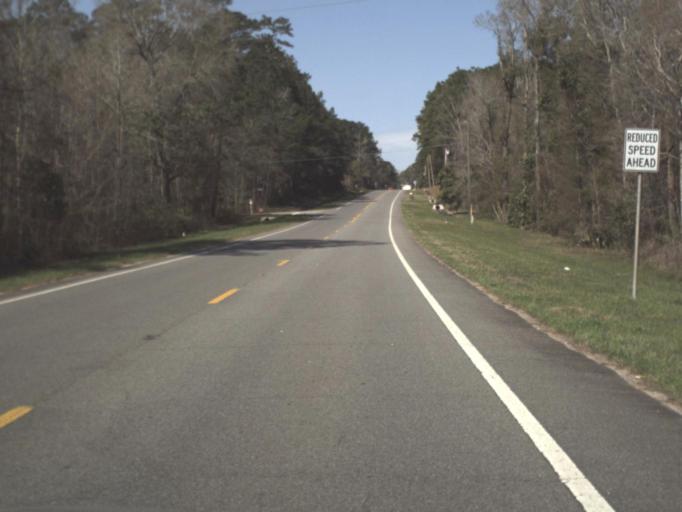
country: US
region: Florida
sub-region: Gadsden County
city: Quincy
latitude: 30.5947
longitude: -84.5306
